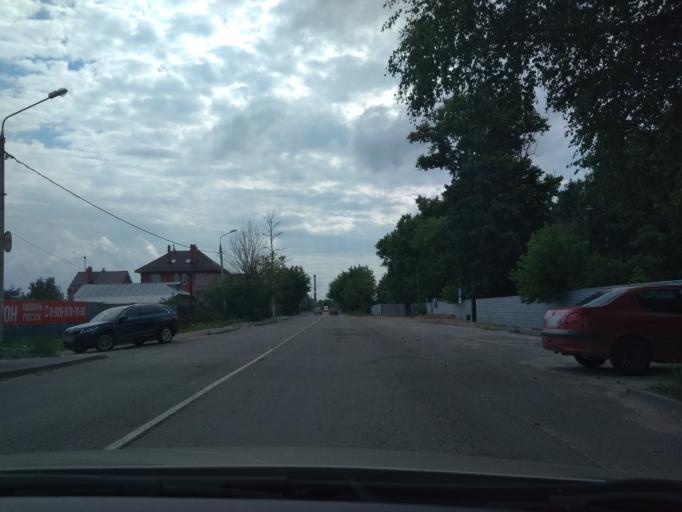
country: RU
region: Moskovskaya
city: Orekhovo-Zuyevo
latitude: 55.8037
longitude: 38.9541
